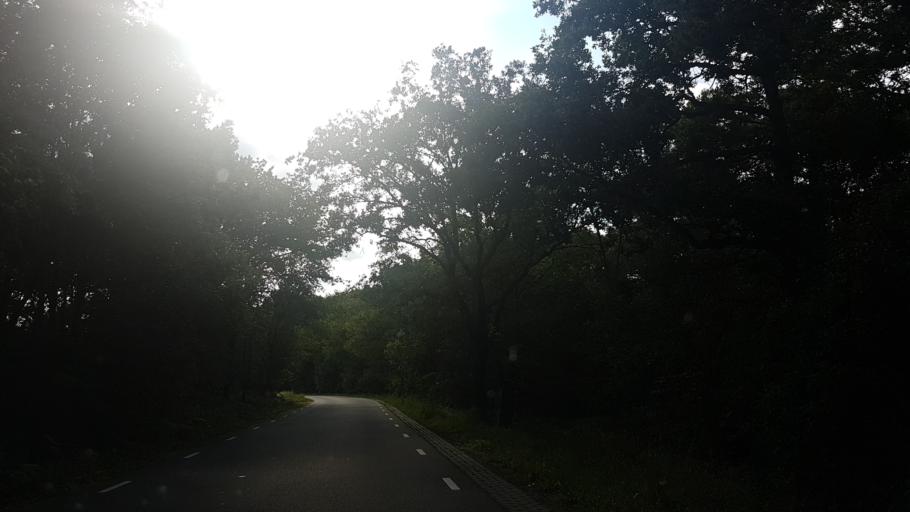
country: NL
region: North Brabant
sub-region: Gemeente Breda
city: Hoge Vucht
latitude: 51.6330
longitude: 4.8111
